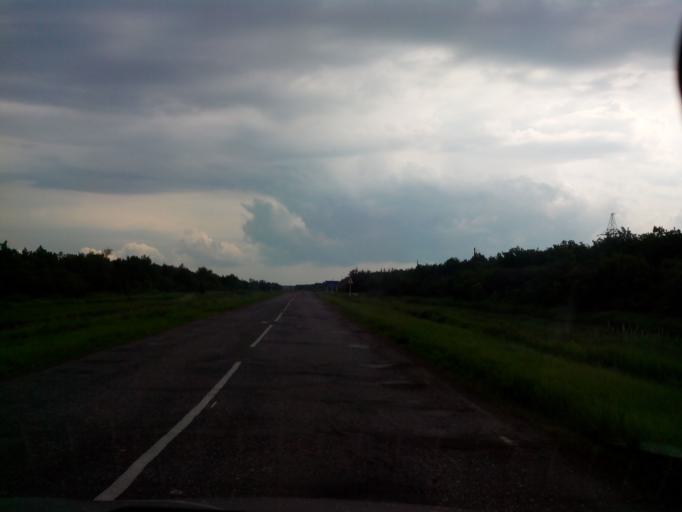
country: RU
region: Volgograd
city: Kumylzhenskaya
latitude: 49.8959
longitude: 42.8214
